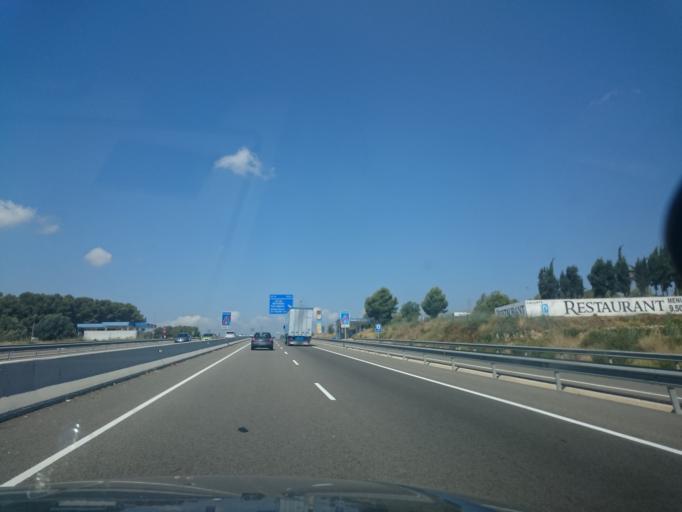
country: ES
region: Catalonia
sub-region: Provincia de Barcelona
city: Vilafranca del Penedes
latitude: 41.3230
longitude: 1.7208
